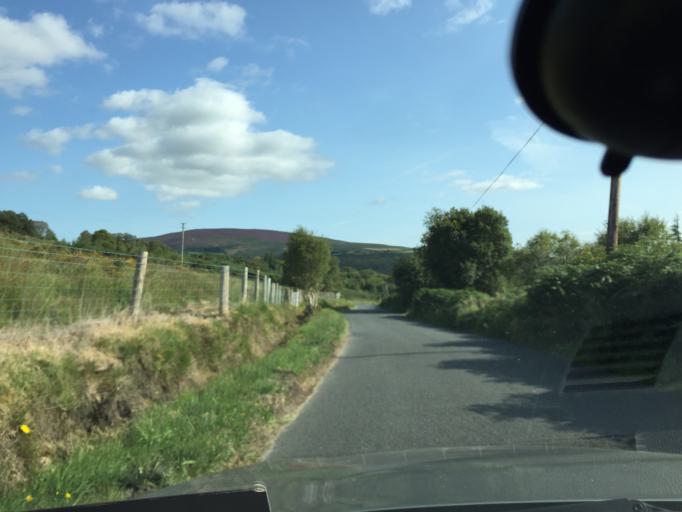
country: IE
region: Leinster
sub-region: Wicklow
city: Rathdrum
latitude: 53.0137
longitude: -6.2984
